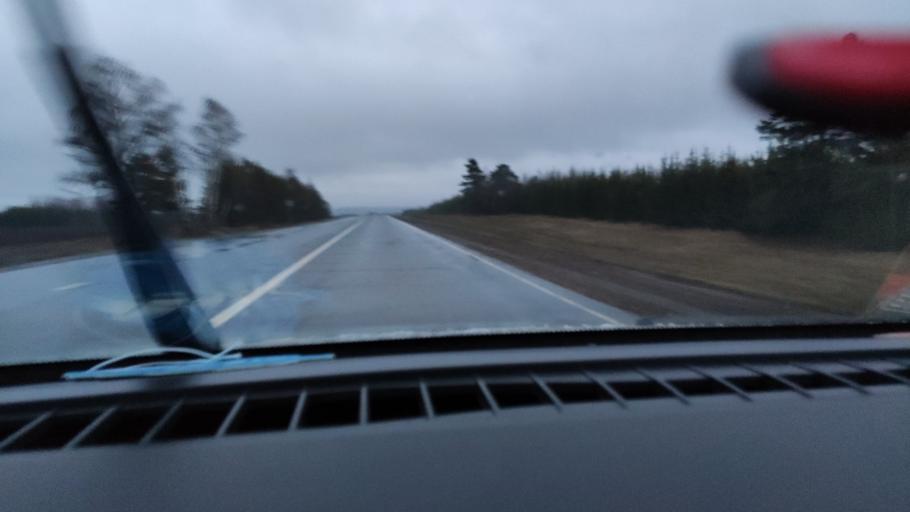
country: RU
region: Udmurtiya
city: Alnashi
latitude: 56.2146
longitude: 52.4302
